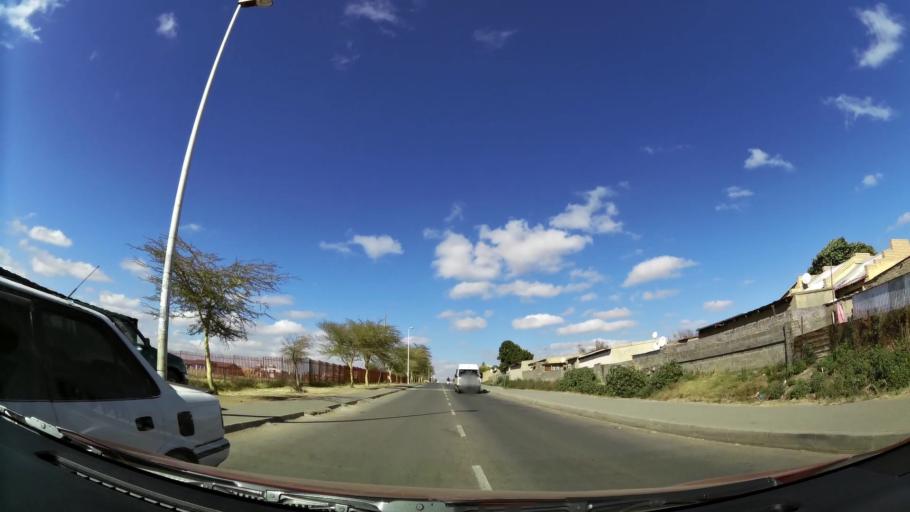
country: ZA
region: Gauteng
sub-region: City of Johannesburg Metropolitan Municipality
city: Modderfontein
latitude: -26.0397
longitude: 28.1814
